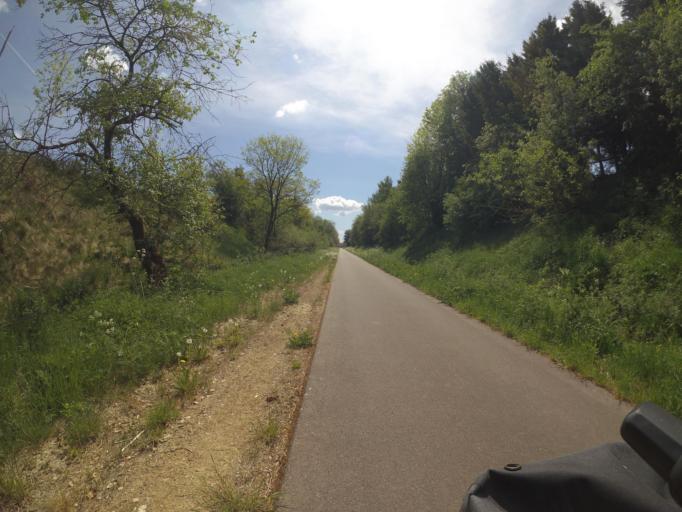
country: BE
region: Wallonia
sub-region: Province de Liege
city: Bullange
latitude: 50.3886
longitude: 6.2756
